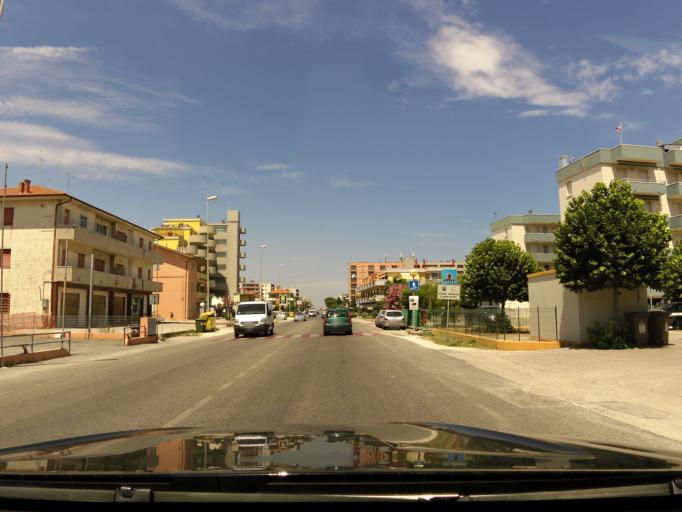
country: IT
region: The Marches
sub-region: Provincia di Pesaro e Urbino
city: Marotta
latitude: 43.7595
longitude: 13.1534
